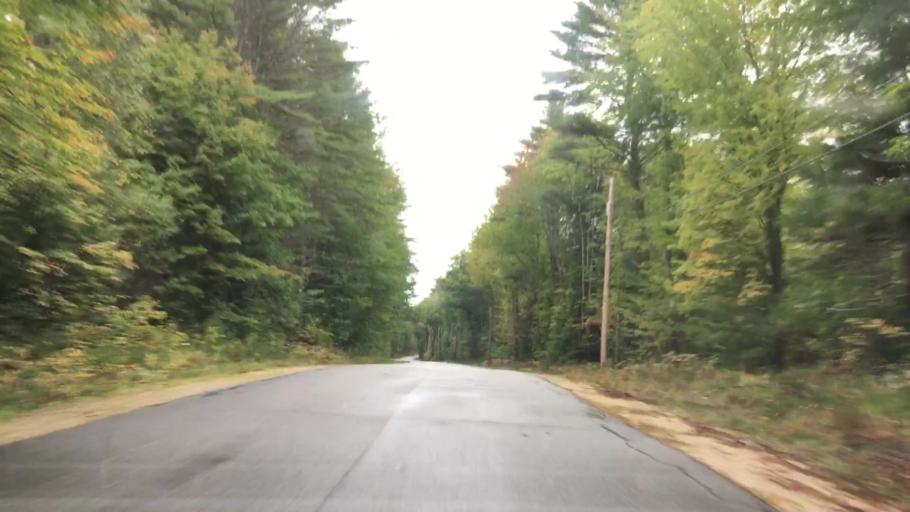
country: US
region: Maine
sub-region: Cumberland County
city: Harrison
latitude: 44.0443
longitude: -70.6125
